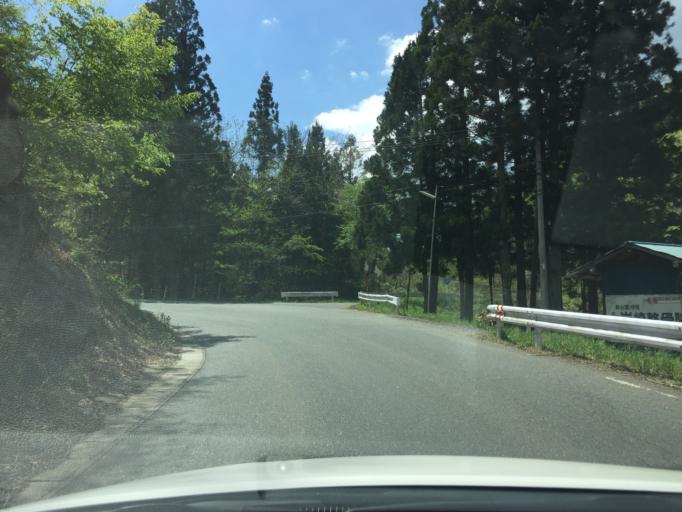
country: JP
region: Fukushima
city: Hobaramachi
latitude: 37.7218
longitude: 140.6433
